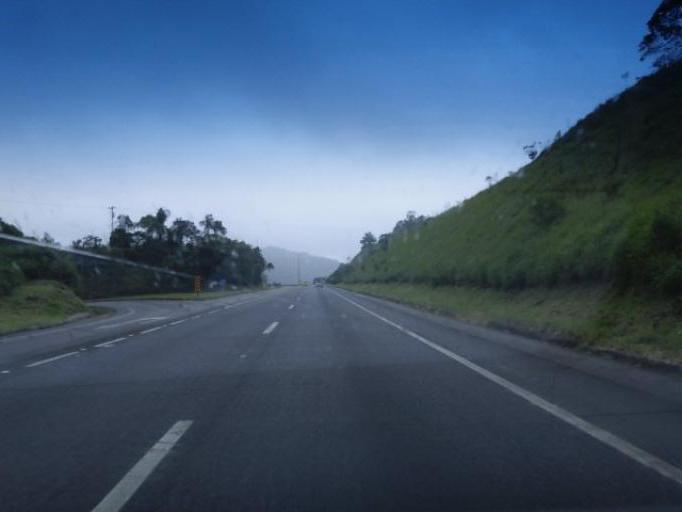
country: BR
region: Parana
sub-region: Antonina
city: Antonina
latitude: -25.0841
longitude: -48.6350
